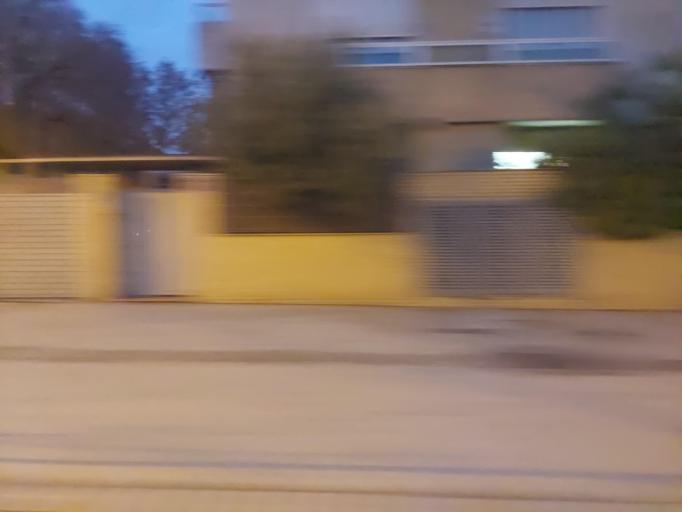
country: ES
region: Madrid
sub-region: Provincia de Madrid
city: Leganes
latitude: 40.3196
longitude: -3.7562
